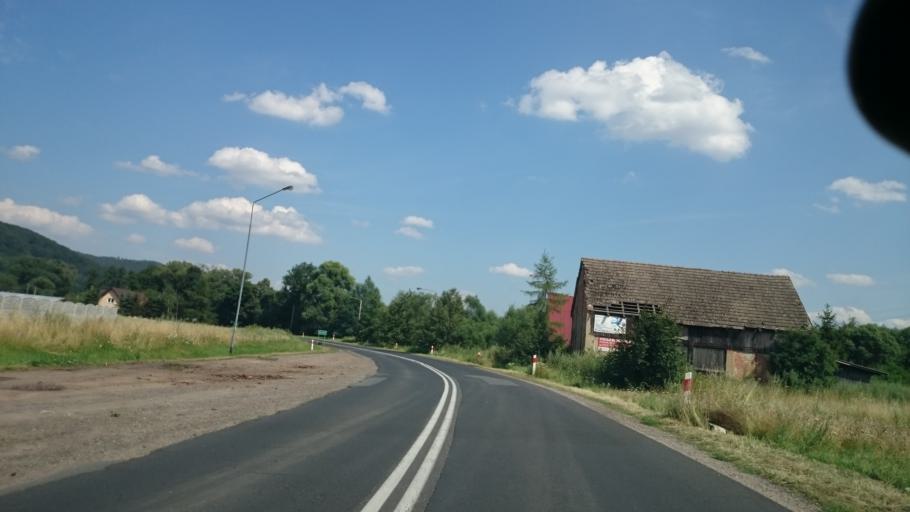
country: PL
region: Lower Silesian Voivodeship
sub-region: Powiat klodzki
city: Klodzko
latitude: 50.3671
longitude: 16.6877
